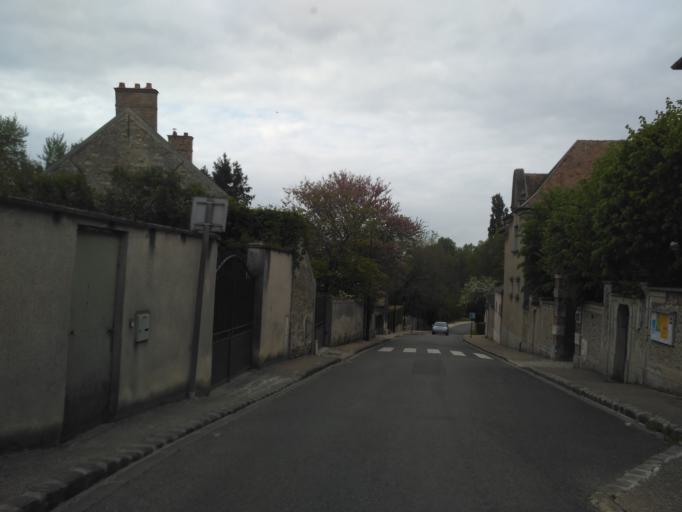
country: FR
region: Ile-de-France
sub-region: Departement de Seine-et-Marne
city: Moisenay
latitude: 48.5688
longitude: 2.7814
